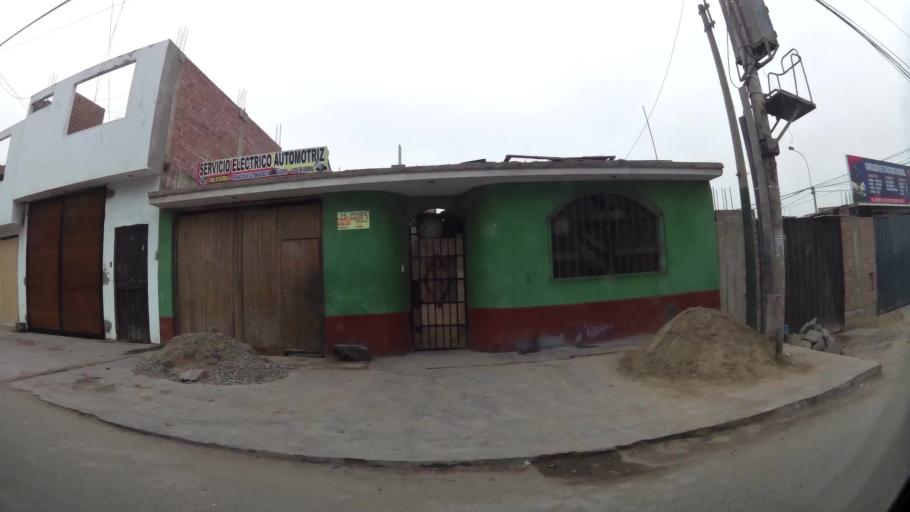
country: PE
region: Lima
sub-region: Lima
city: Surco
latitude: -12.1976
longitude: -76.9772
